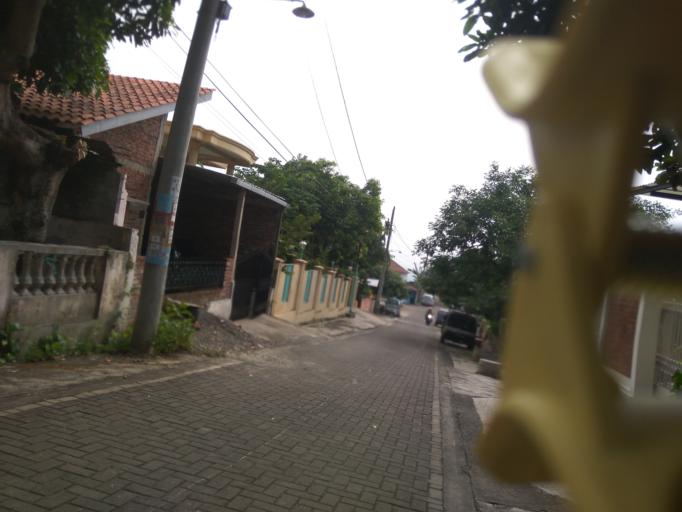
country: ID
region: Central Java
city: Semarang
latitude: -7.0432
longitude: 110.4193
